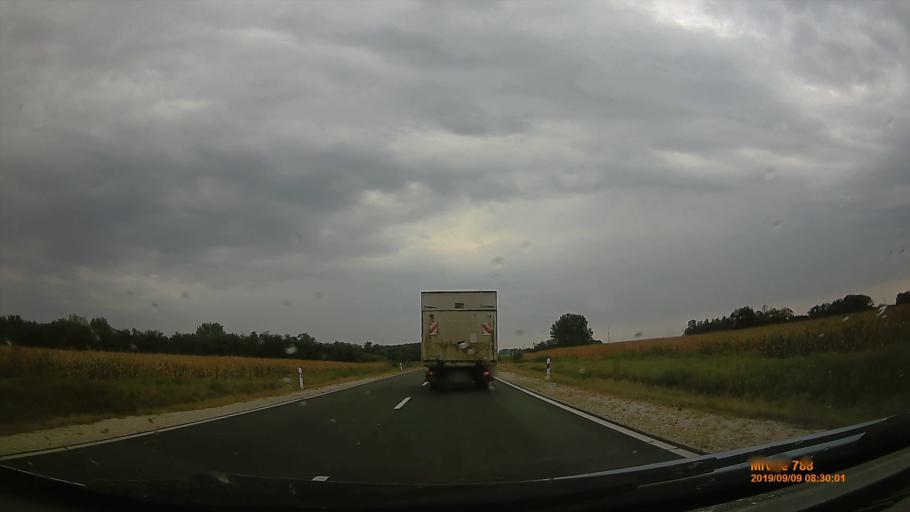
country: HU
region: Szabolcs-Szatmar-Bereg
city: Nyiregyhaza
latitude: 47.9367
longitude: 21.6484
